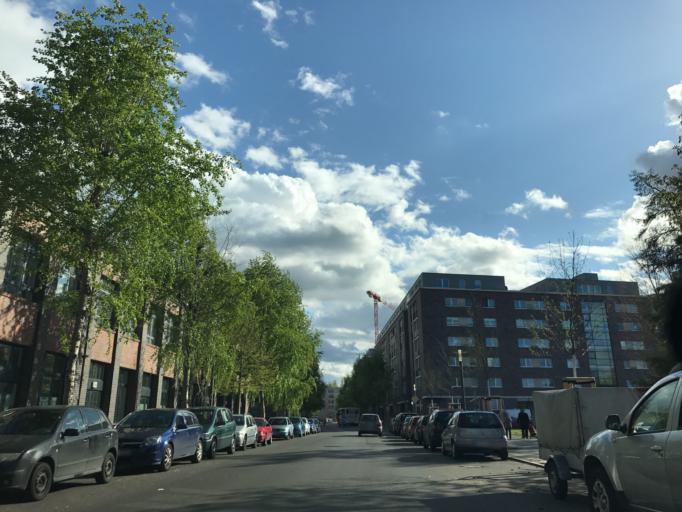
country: DE
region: Berlin
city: Hakenfelde
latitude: 52.5594
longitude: 13.2188
